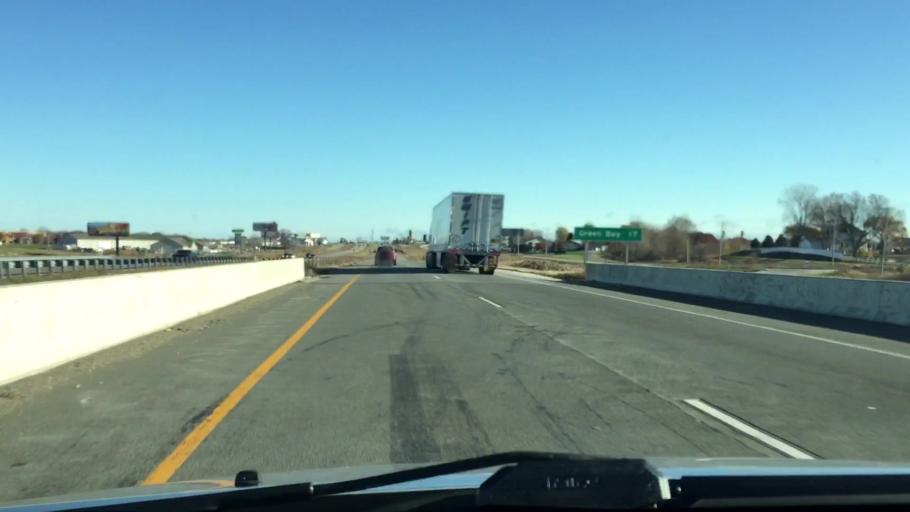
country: US
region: Wisconsin
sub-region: Outagamie County
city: Kaukauna
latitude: 44.3141
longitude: -88.2286
